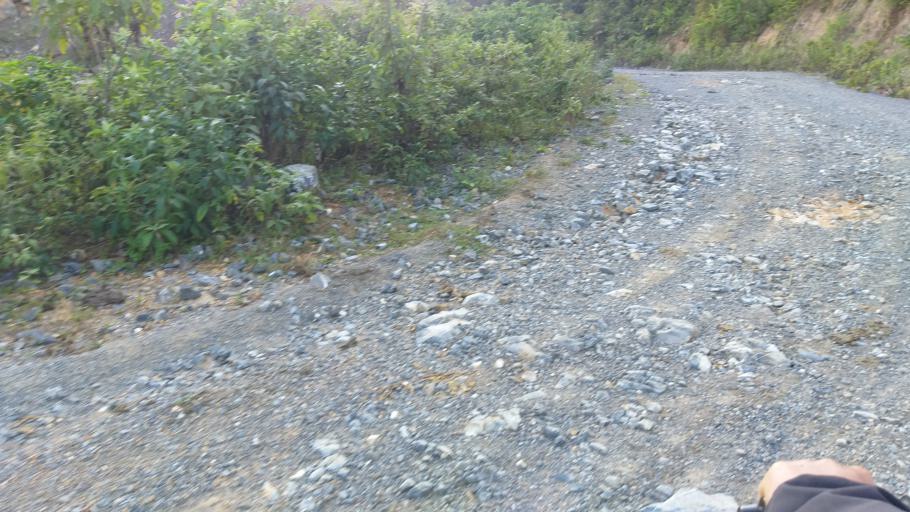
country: LA
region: Phongsali
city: Khoa
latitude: 21.2220
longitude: 102.5977
